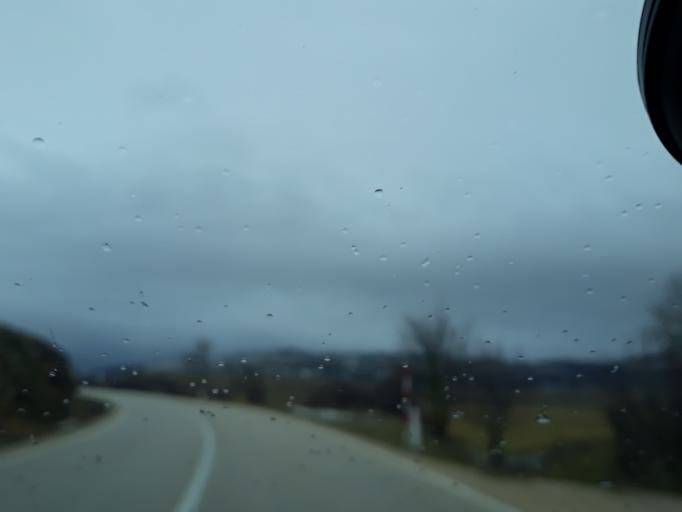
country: BA
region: Federation of Bosnia and Herzegovina
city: Tomislavgrad
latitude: 43.8333
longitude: 17.1875
